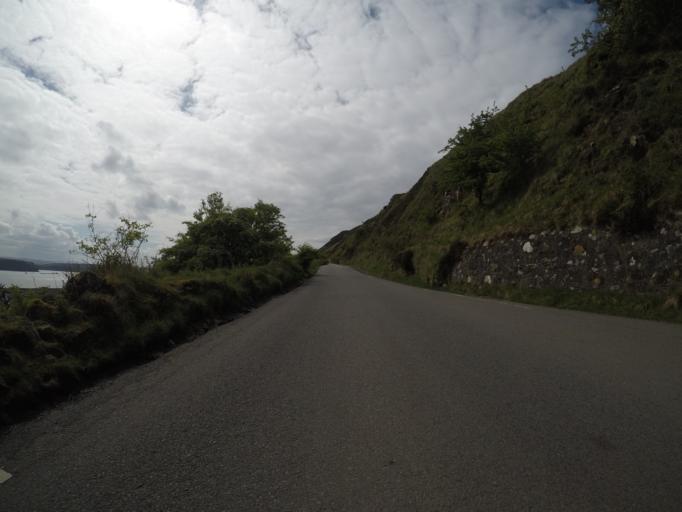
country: GB
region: Scotland
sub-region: Highland
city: Portree
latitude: 57.5924
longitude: -6.3749
